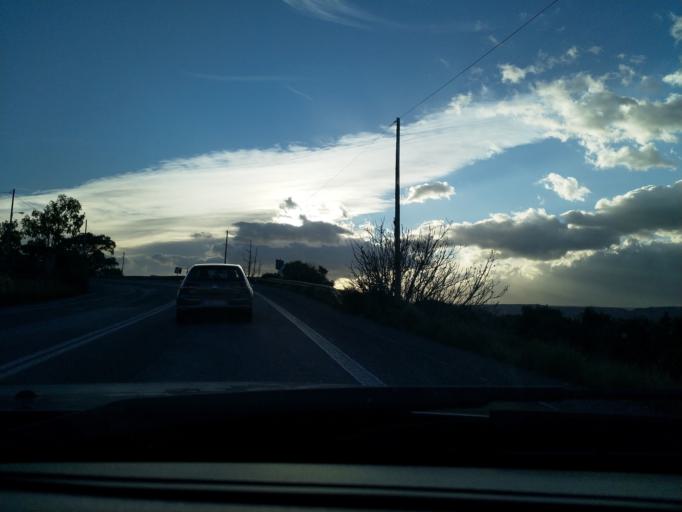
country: GR
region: Crete
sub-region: Nomos Chanias
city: Pithari
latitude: 35.5167
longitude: 24.0947
